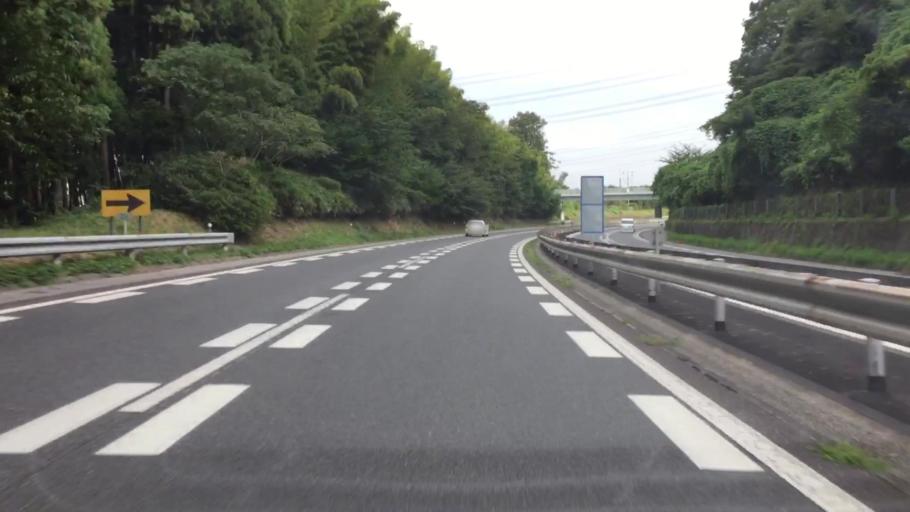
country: JP
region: Tochigi
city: Utsunomiya-shi
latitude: 36.6651
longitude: 139.8329
